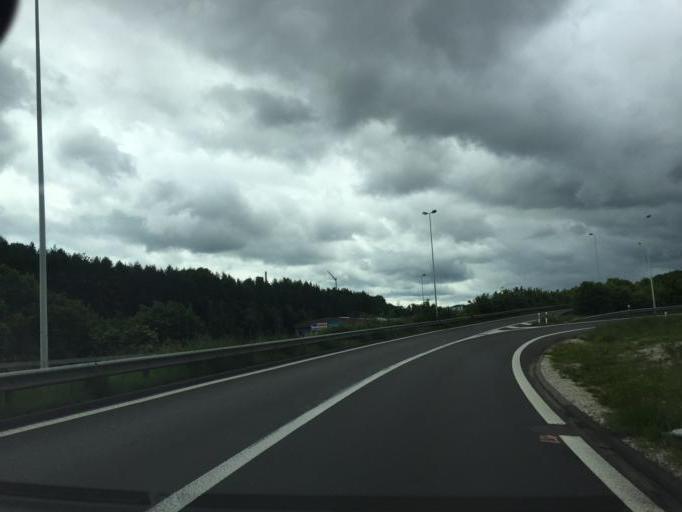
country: CH
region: Schaffhausen
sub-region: Bezirk Schaffhausen
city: Schaffhausen
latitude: 47.7148
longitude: 8.6530
